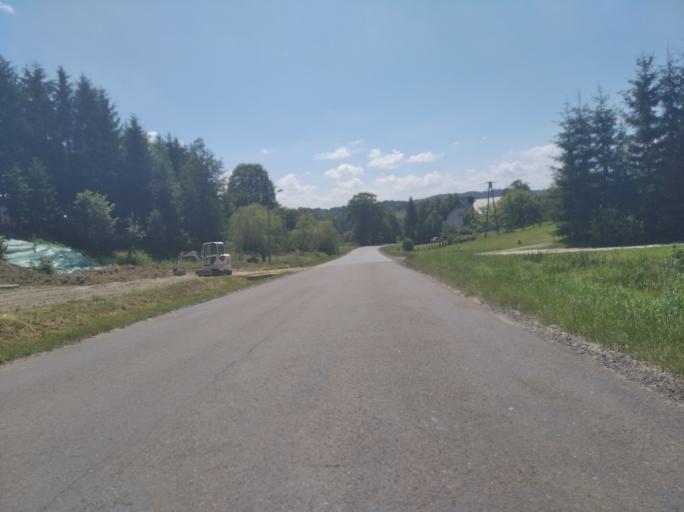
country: PL
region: Subcarpathian Voivodeship
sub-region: Powiat brzozowski
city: Jablonka
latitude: 49.6864
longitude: 22.1174
